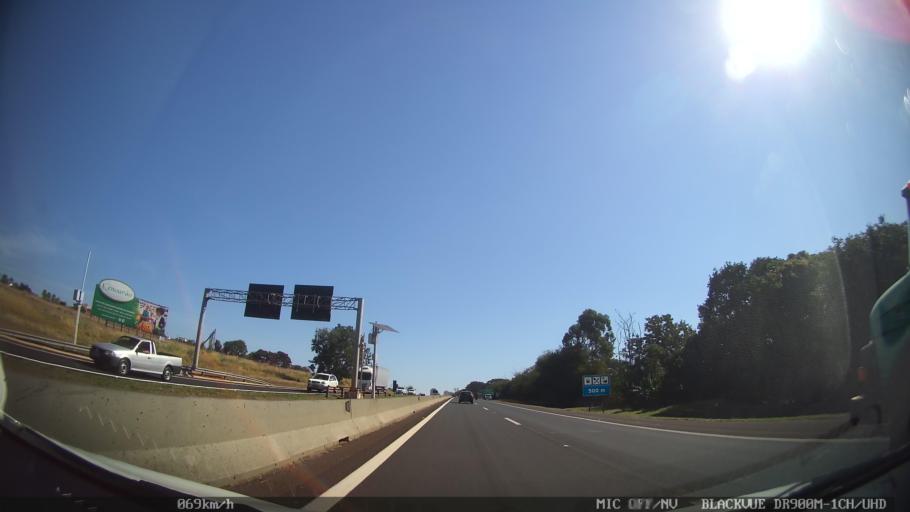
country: BR
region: Sao Paulo
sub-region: Ribeirao Preto
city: Ribeirao Preto
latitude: -21.2217
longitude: -47.7815
